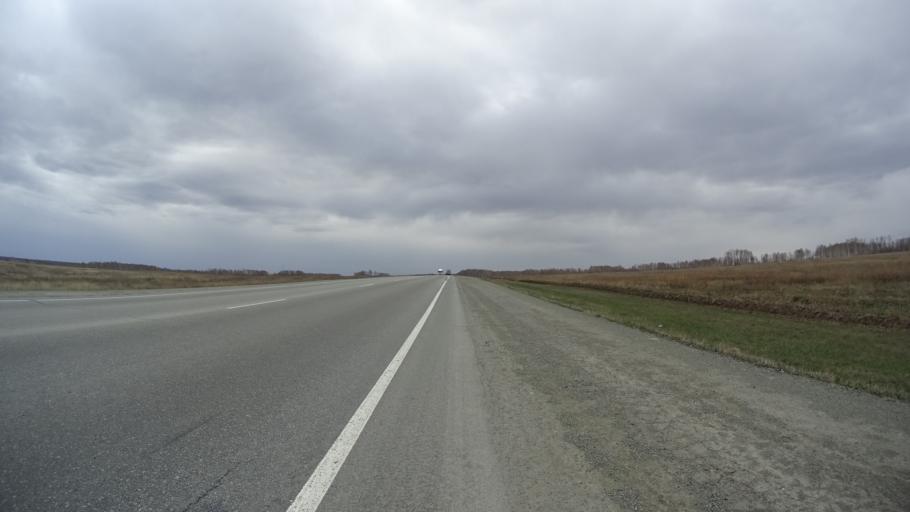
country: RU
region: Chelyabinsk
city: Yemanzhelinsk
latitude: 54.7064
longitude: 61.2569
